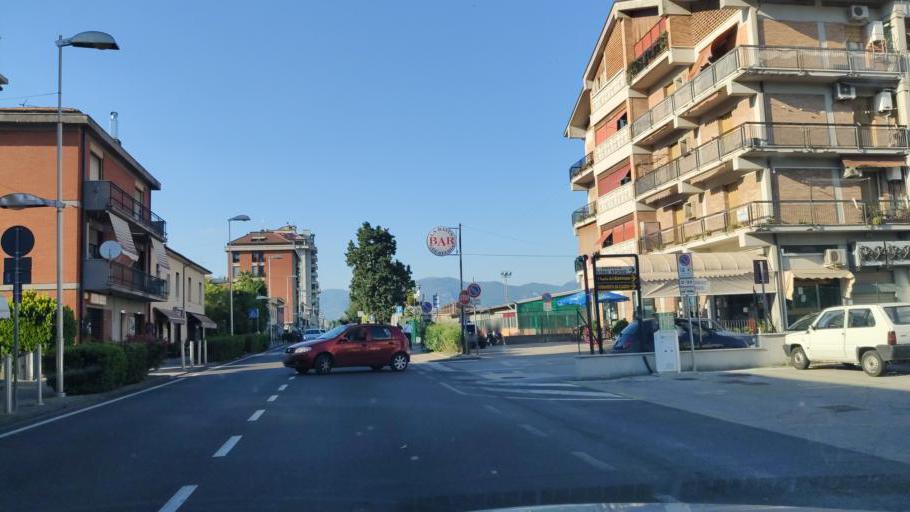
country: IT
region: Umbria
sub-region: Provincia di Terni
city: Narni Scalo
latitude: 42.5327
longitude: 12.5181
